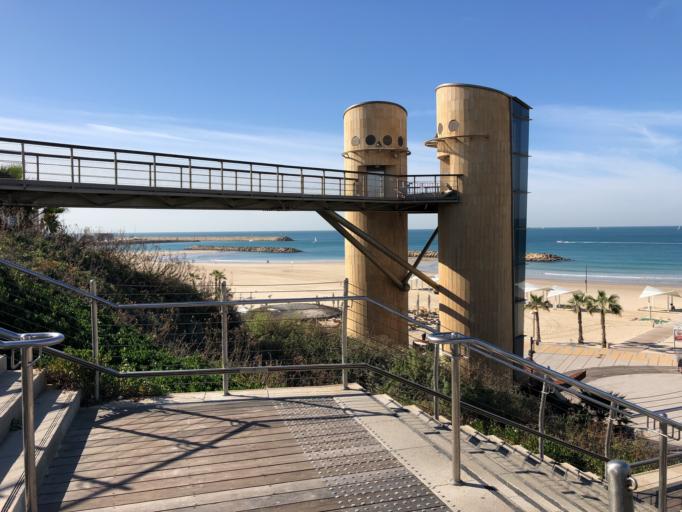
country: IL
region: Tel Aviv
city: Herzliya Pituah
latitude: 32.1703
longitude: 34.8001
